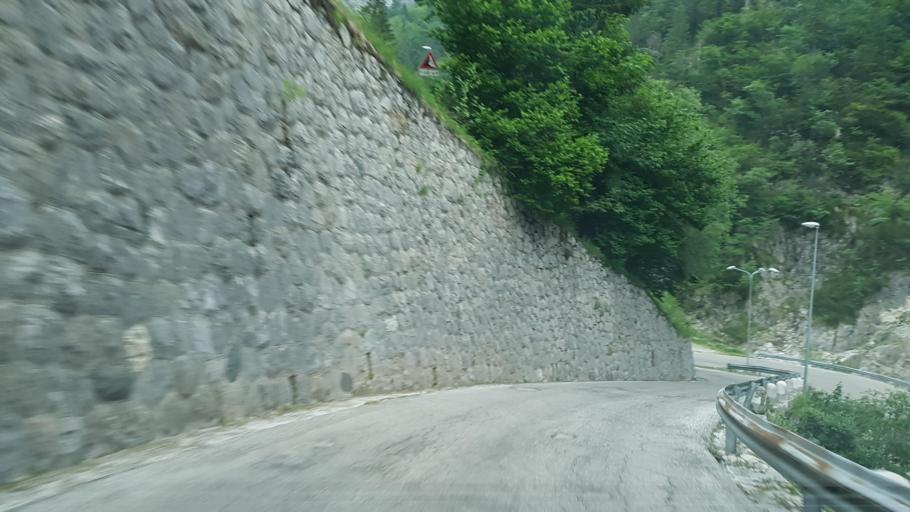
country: IT
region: Friuli Venezia Giulia
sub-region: Provincia di Udine
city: Pontebba
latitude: 46.5300
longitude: 13.3042
